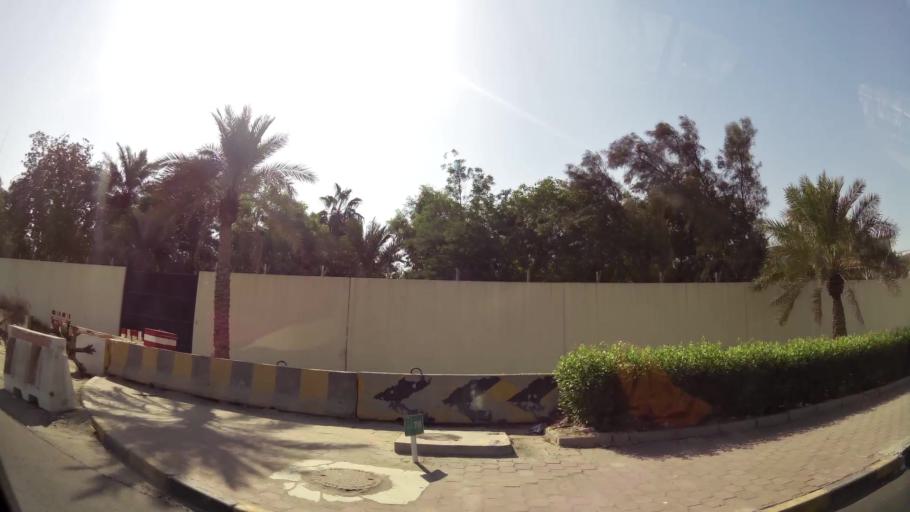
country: KW
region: Al Asimah
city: Ad Dasmah
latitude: 29.3908
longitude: 47.9949
